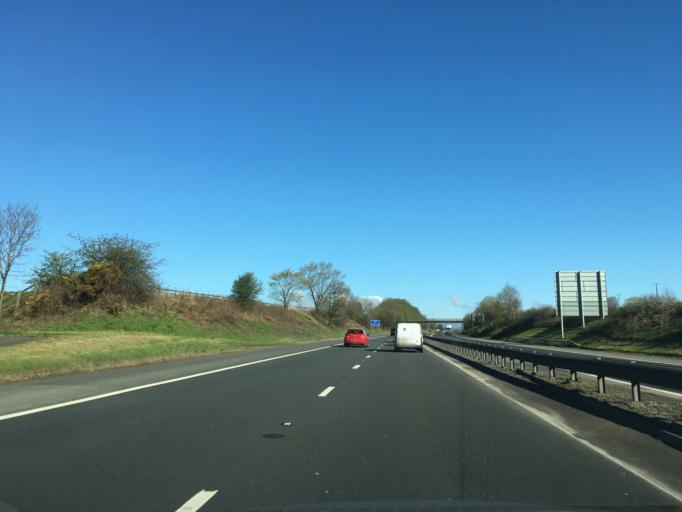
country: GB
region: Scotland
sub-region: Stirling
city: Stirling
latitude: 56.0898
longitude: -3.9467
